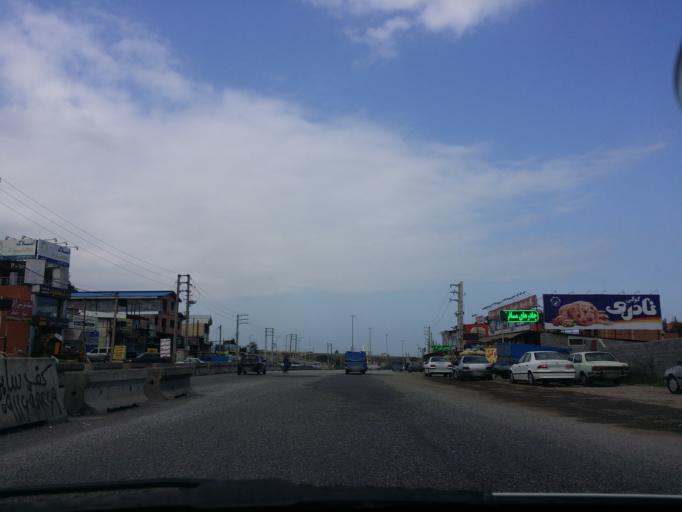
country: IR
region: Mazandaran
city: Chalus
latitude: 36.6489
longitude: 51.4090
